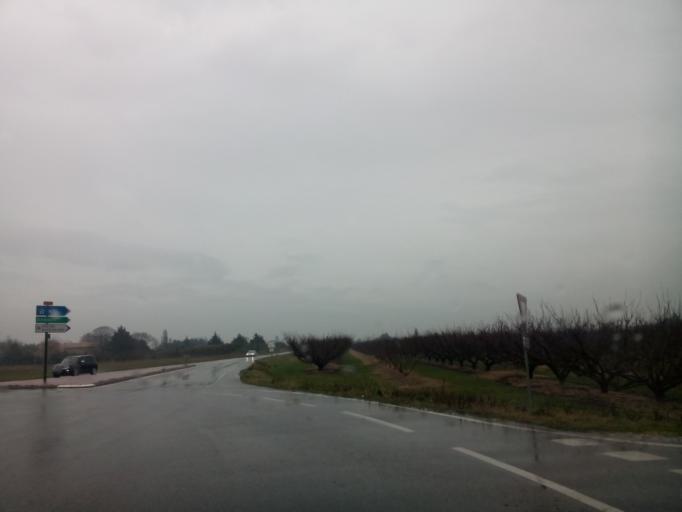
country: FR
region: Rhone-Alpes
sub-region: Departement de la Drome
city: Clerieux
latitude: 45.0476
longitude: 4.9961
